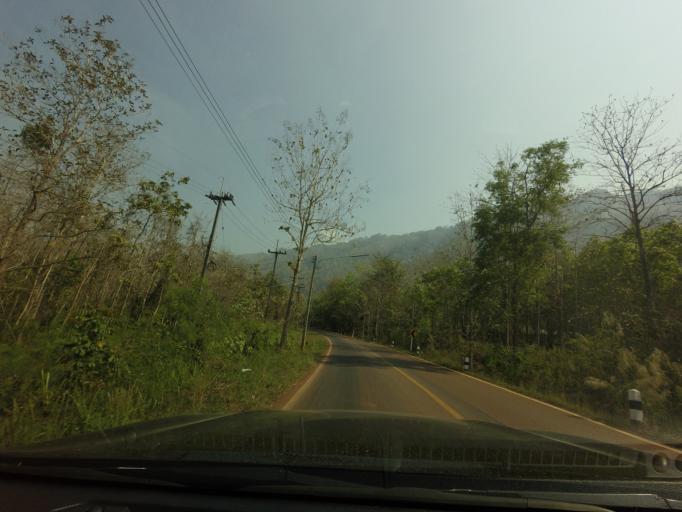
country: TH
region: Kanchanaburi
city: Thong Pha Phum
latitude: 14.6562
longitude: 98.6034
